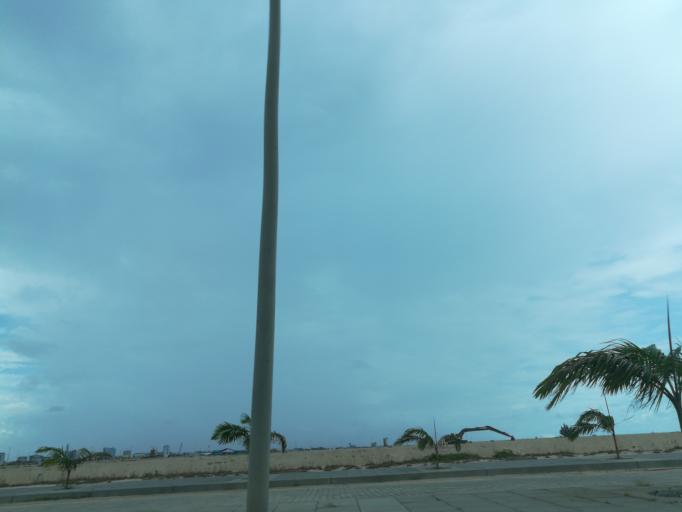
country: NG
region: Lagos
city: Ikoyi
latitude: 6.4081
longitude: 3.4206
